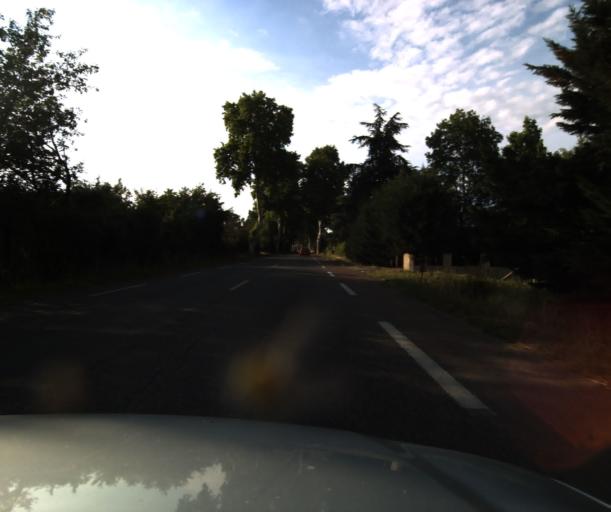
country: FR
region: Midi-Pyrenees
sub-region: Departement du Tarn-et-Garonne
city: Moissac
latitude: 44.0695
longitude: 1.0951
